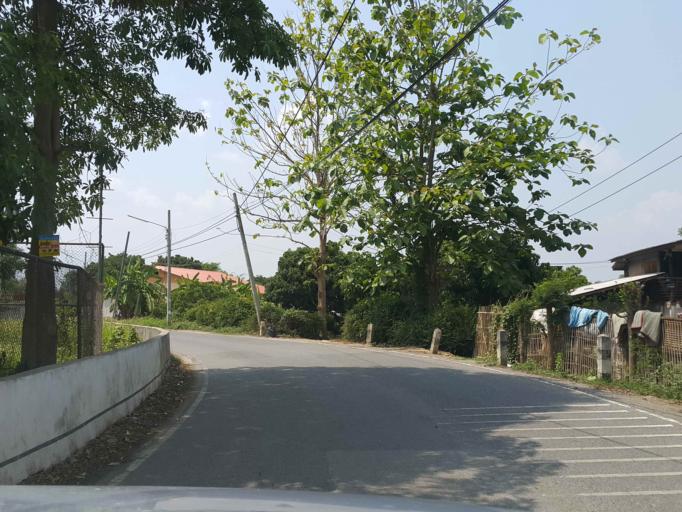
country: TH
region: Chiang Mai
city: Saraphi
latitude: 18.6998
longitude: 98.9869
